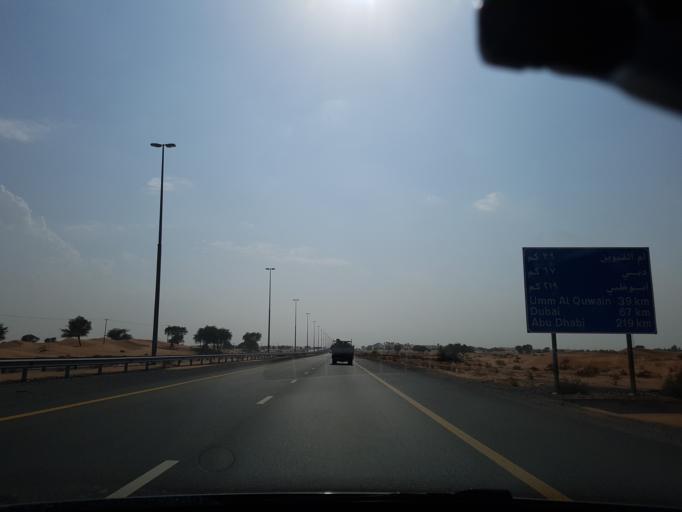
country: AE
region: Umm al Qaywayn
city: Umm al Qaywayn
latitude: 25.5223
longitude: 55.7555
